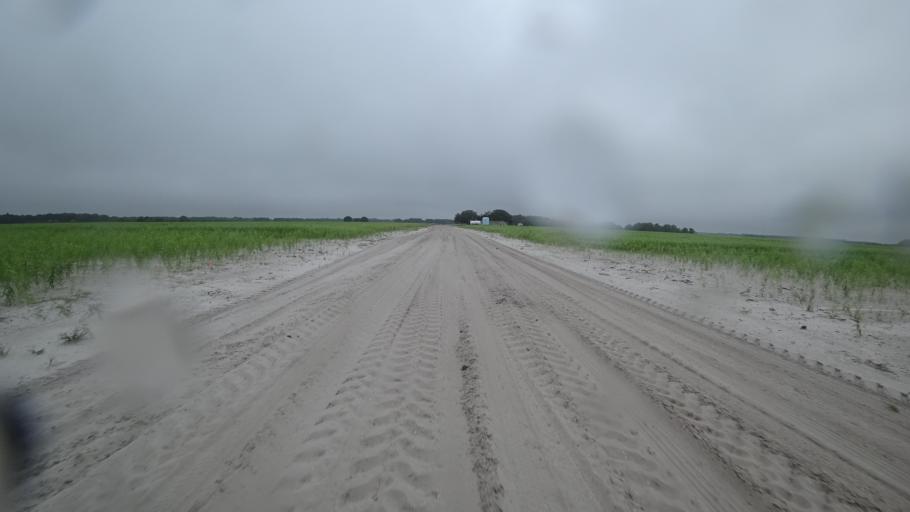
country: US
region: Florida
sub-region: Sarasota County
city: Warm Mineral Springs
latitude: 27.2947
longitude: -82.1608
